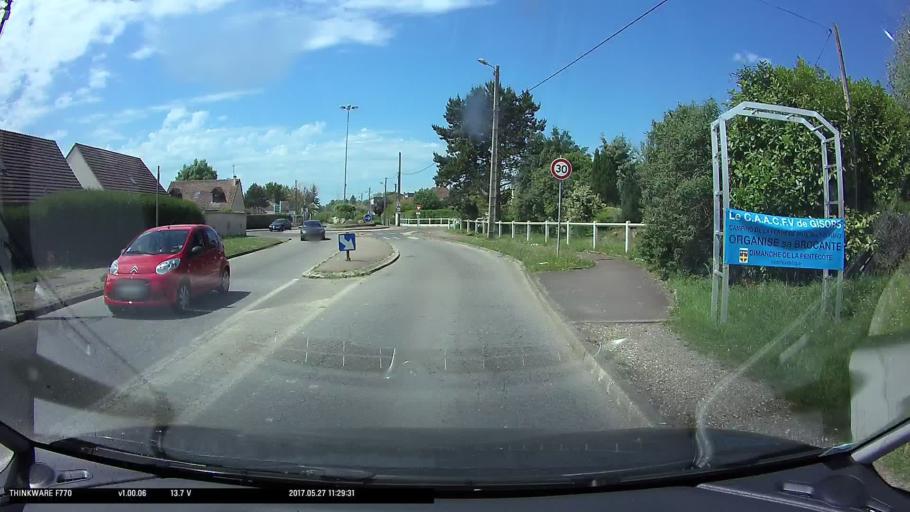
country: FR
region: Haute-Normandie
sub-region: Departement de l'Eure
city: Gisors
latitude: 49.2866
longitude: 1.7950
